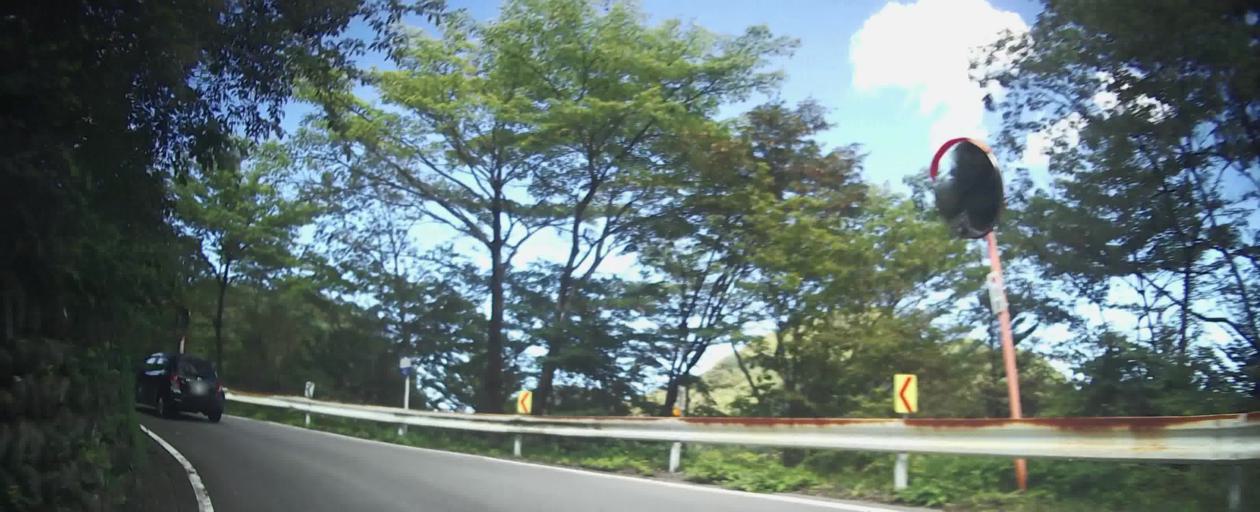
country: JP
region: Gunma
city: Shibukawa
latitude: 36.4661
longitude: 138.8893
